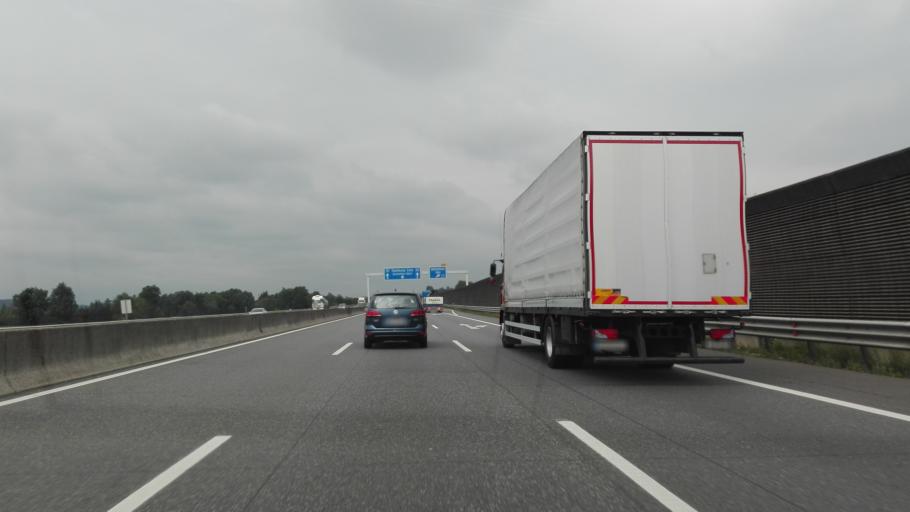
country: AT
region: Lower Austria
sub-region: Politischer Bezirk Melk
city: Neumarkt an der Ybbs
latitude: 48.1303
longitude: 15.0228
